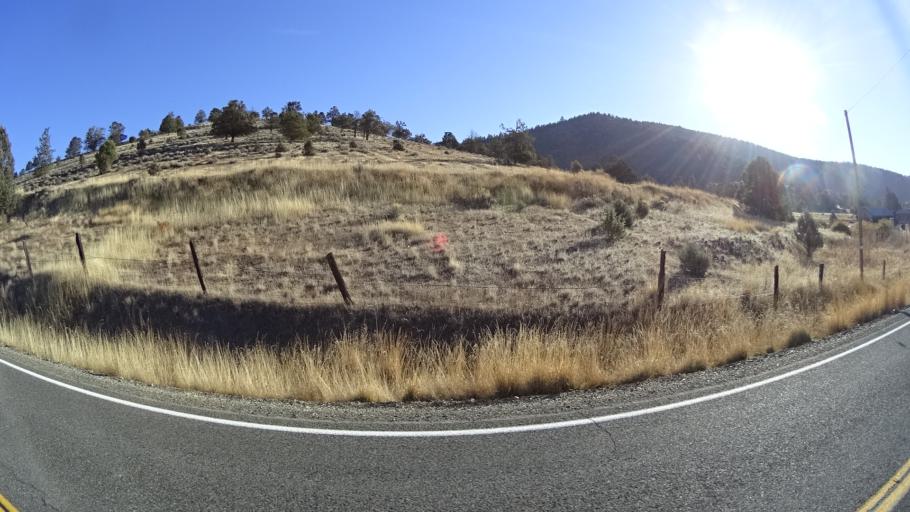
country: US
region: California
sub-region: Siskiyou County
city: Yreka
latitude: 41.5270
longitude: -122.8427
